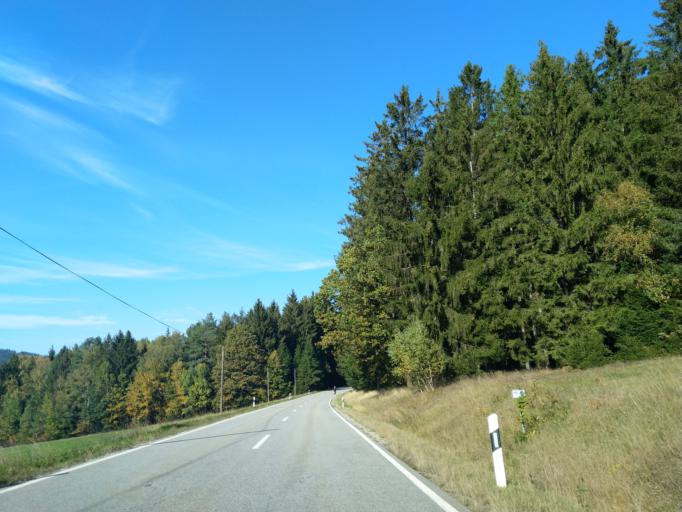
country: DE
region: Bavaria
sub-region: Lower Bavaria
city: Achslach
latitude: 48.9605
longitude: 12.9273
